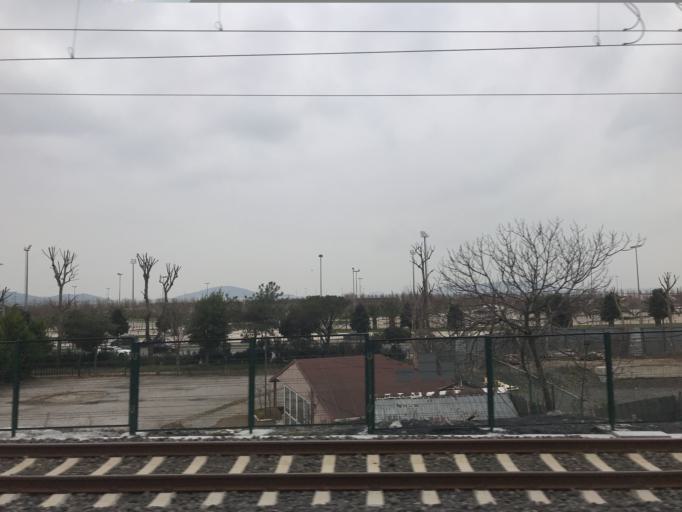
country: TR
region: Istanbul
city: Maltepe
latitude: 40.9313
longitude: 29.1197
